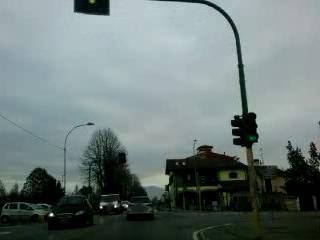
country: IT
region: Lombardy
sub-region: Provincia di Brescia
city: Capriano del Colle
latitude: 45.4737
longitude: 10.1286
